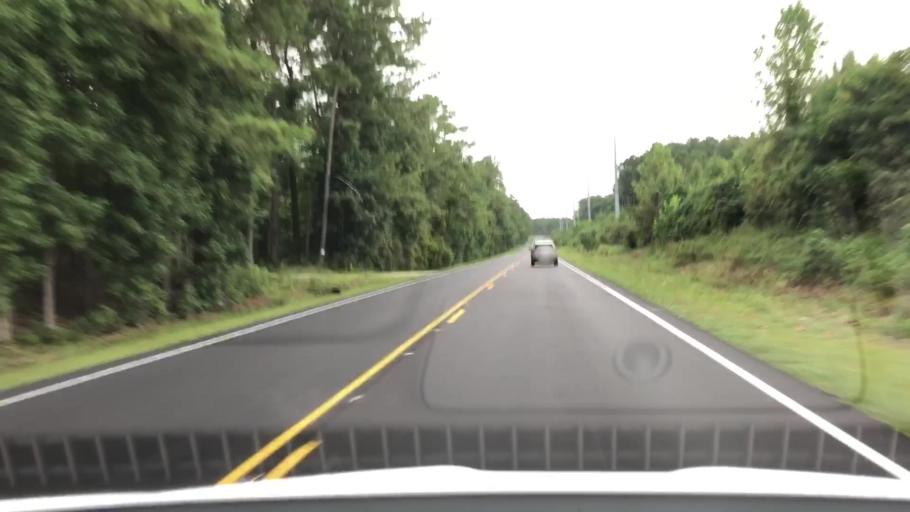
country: US
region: North Carolina
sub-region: Carteret County
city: Cape Carteret
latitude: 34.7626
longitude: -77.0954
